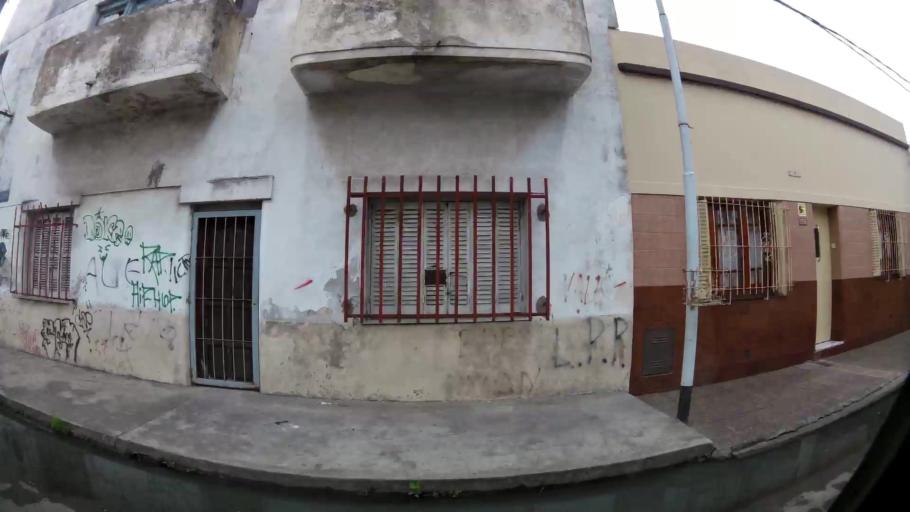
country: AR
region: Buenos Aires
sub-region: Partido de Avellaneda
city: Avellaneda
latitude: -34.6532
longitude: -58.3471
